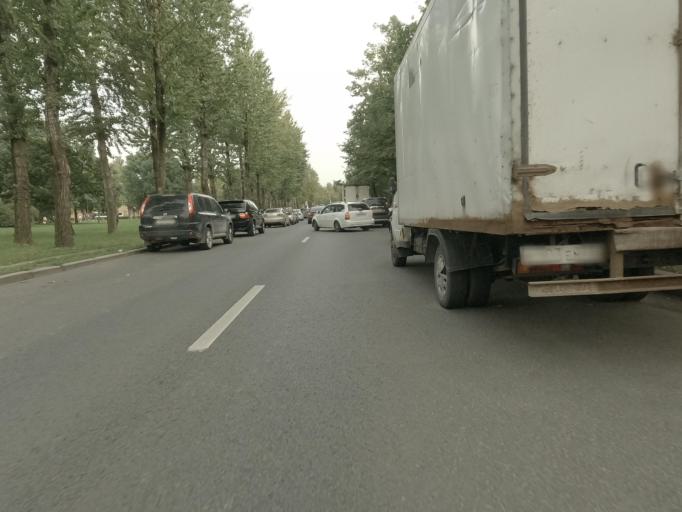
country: RU
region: St.-Petersburg
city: Dachnoye
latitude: 59.8473
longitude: 30.2678
